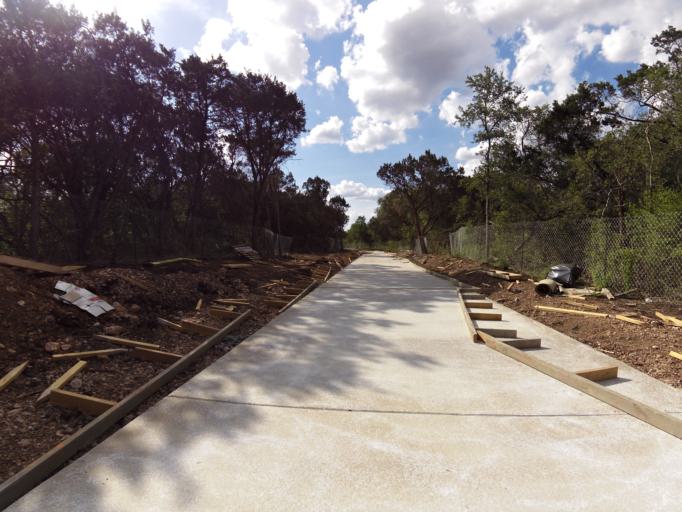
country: US
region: Texas
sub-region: Bexar County
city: Shavano Park
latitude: 29.5981
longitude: -98.5965
